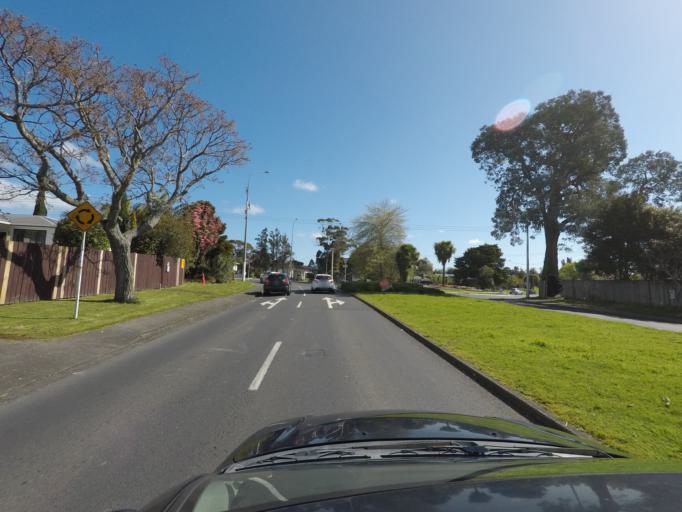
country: NZ
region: Auckland
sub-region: Auckland
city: Rosebank
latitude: -36.8606
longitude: 174.6125
